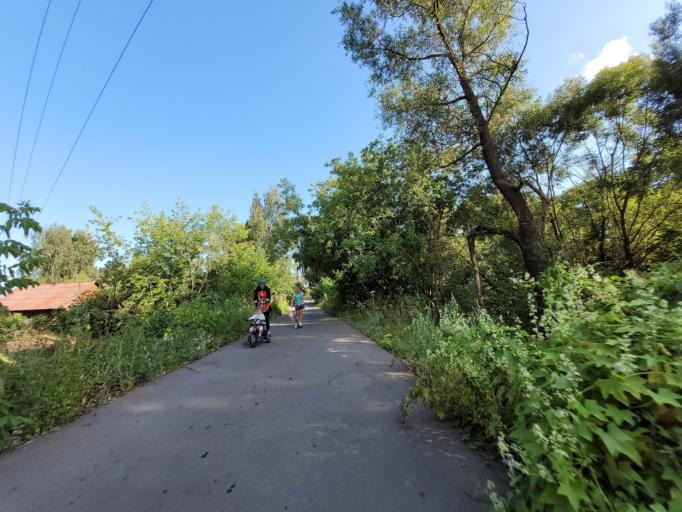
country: RU
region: Moskovskaya
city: Konobeyevo
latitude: 55.4130
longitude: 38.6949
